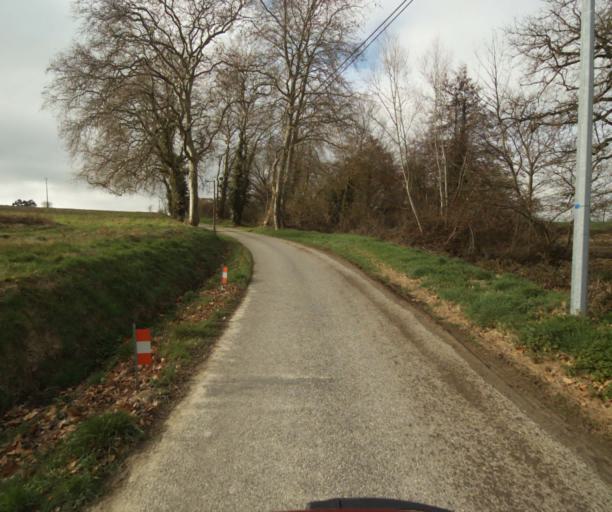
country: FR
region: Languedoc-Roussillon
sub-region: Departement de l'Aude
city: Belpech
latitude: 43.1777
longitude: 1.7236
